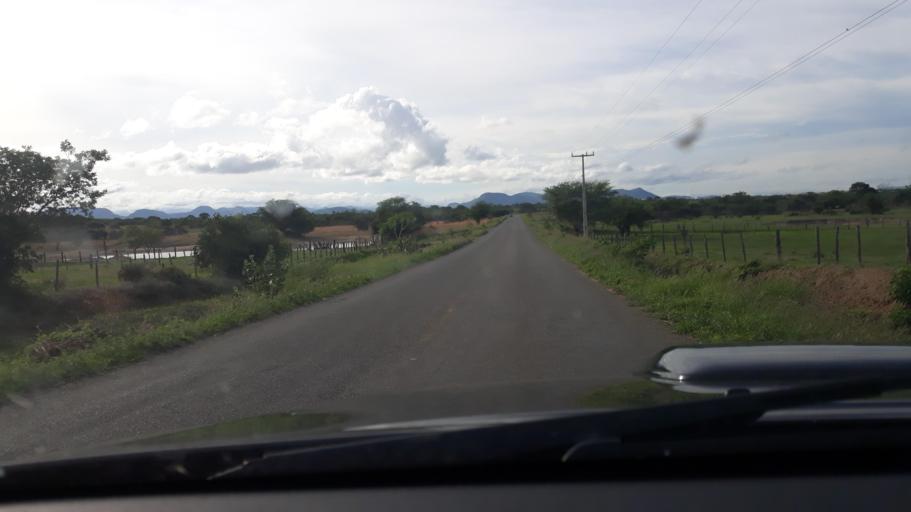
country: BR
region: Bahia
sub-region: Guanambi
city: Guanambi
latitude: -14.1774
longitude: -42.8003
